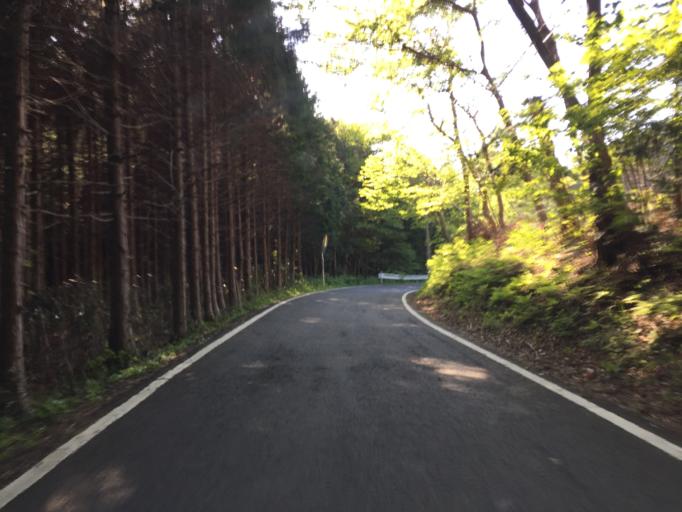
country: JP
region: Ibaraki
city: Kitaibaraki
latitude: 36.8938
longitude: 140.6035
